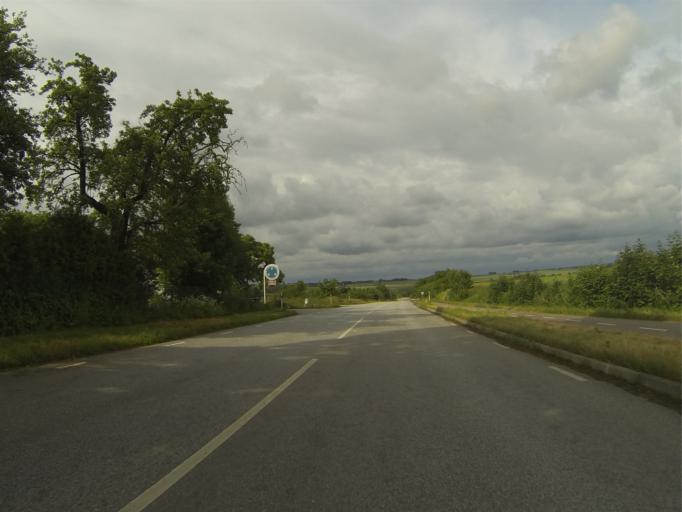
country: SE
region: Skane
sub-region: Eslovs Kommun
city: Eslov
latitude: 55.7606
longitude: 13.3079
